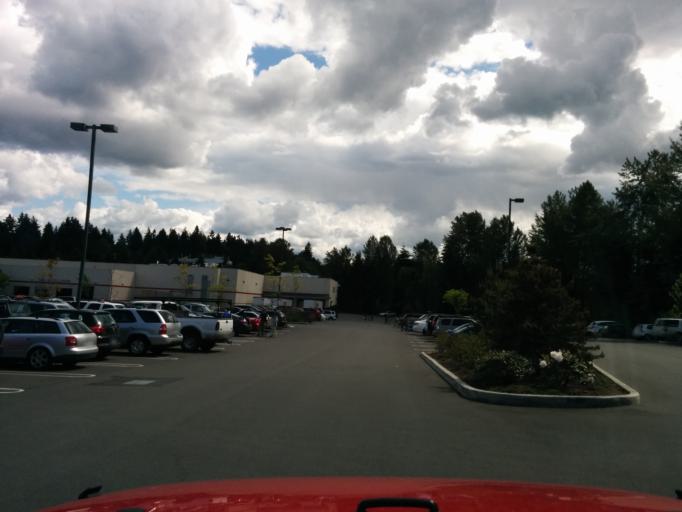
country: US
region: Washington
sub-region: King County
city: Kirkland
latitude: 47.6822
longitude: -122.1829
